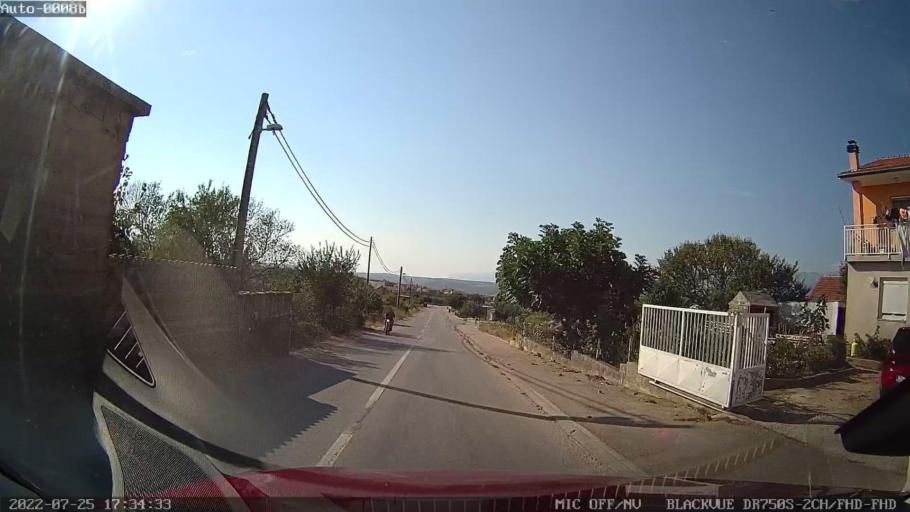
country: HR
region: Zadarska
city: Posedarje
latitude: 44.1845
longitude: 15.4769
